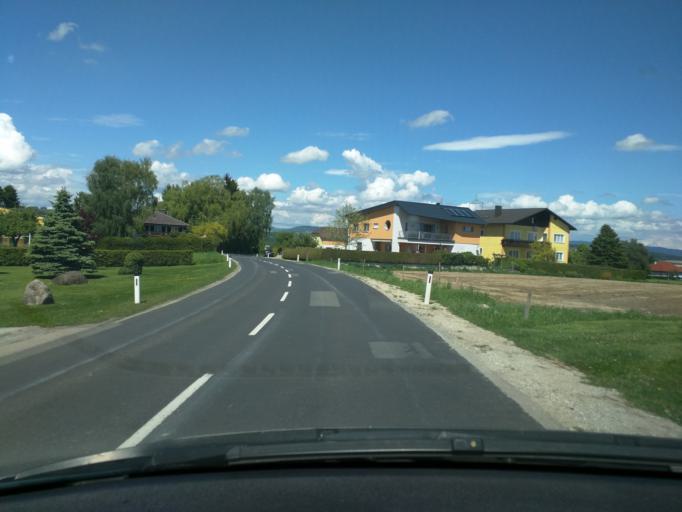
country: AT
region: Lower Austria
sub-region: Politischer Bezirk Amstetten
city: Amstetten
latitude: 48.1503
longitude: 14.8957
